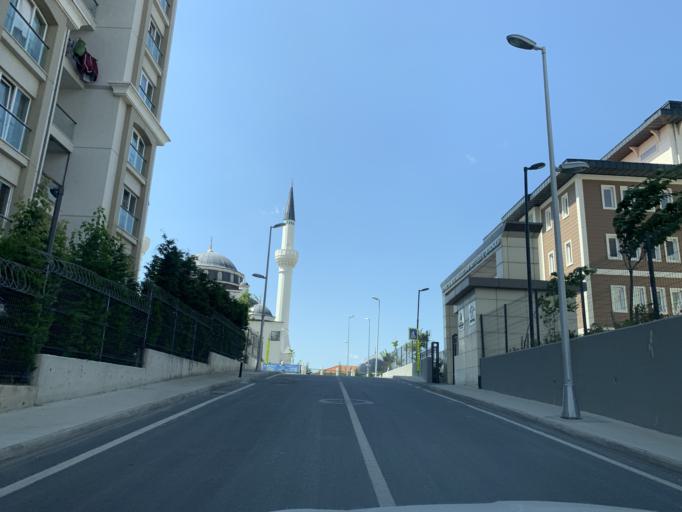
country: TR
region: Istanbul
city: Esenyurt
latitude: 41.0818
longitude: 28.6930
